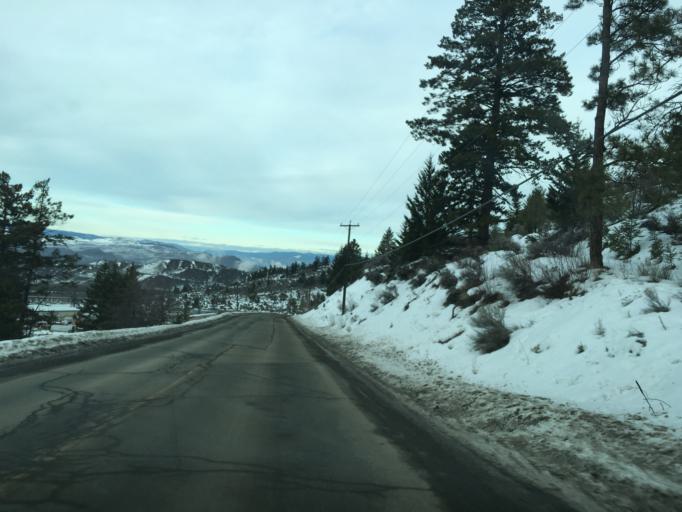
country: CA
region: British Columbia
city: Kamloops
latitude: 50.6561
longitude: -120.4378
